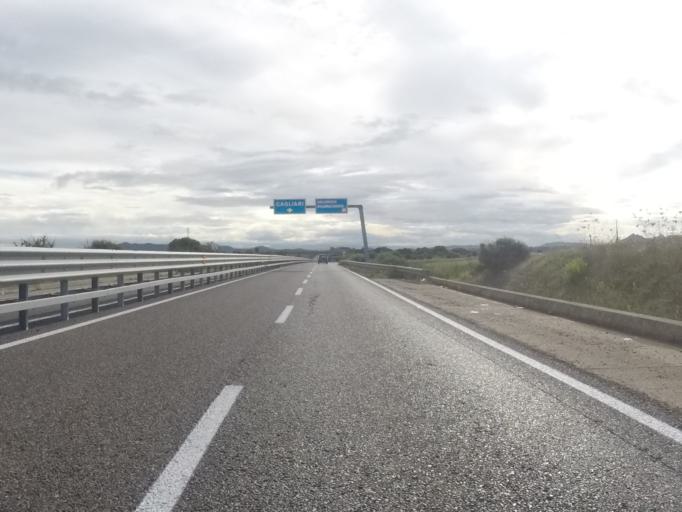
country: IT
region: Sardinia
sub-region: Provincia di Cagliari
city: Siliqua
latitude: 39.3048
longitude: 8.7374
